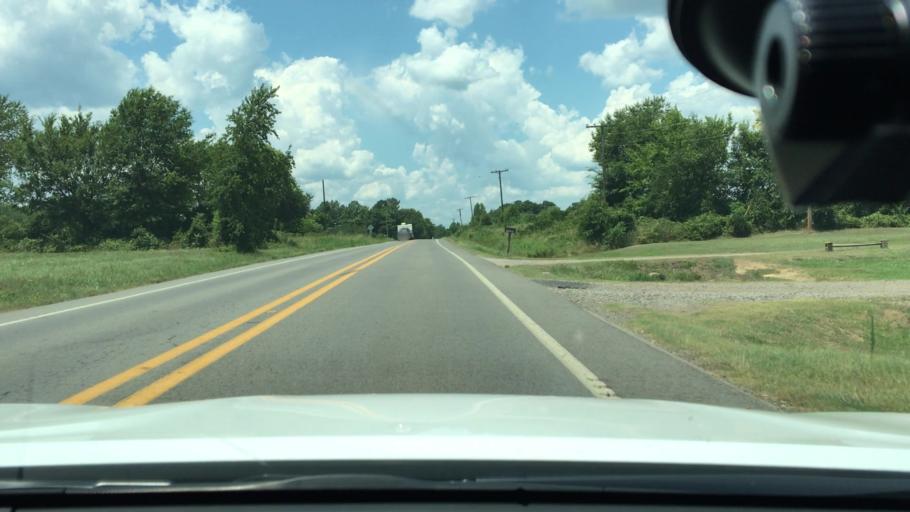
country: US
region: Arkansas
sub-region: Logan County
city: Booneville
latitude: 35.1478
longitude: -93.8364
